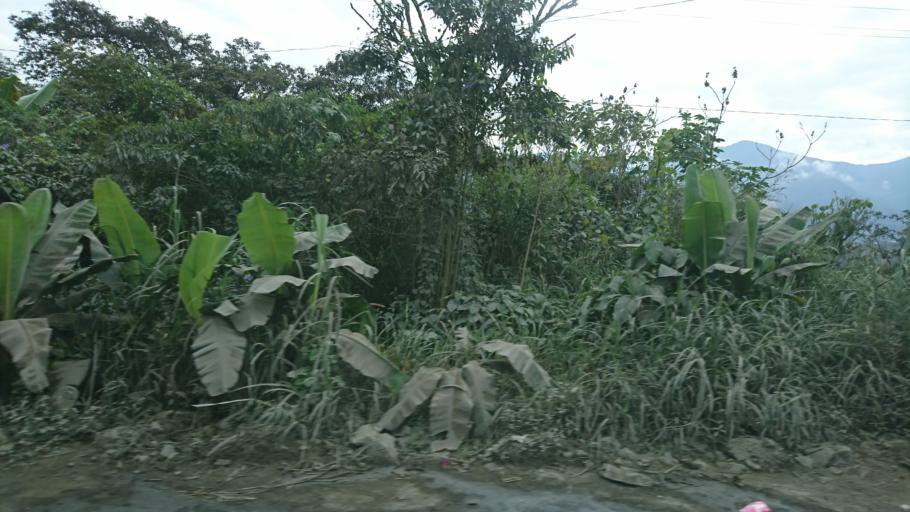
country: BO
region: La Paz
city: Coroico
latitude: -16.2000
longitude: -67.7021
